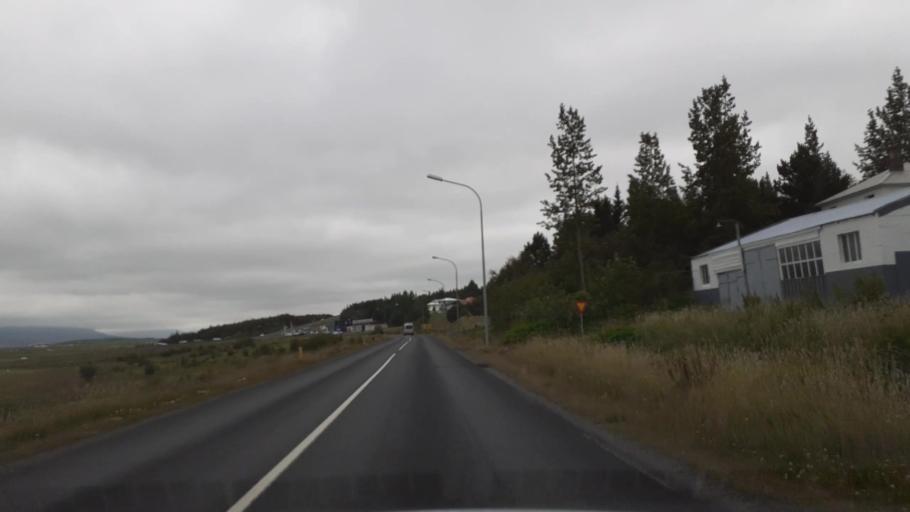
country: IS
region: Northwest
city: Saudarkrokur
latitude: 65.5568
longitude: -19.4511
